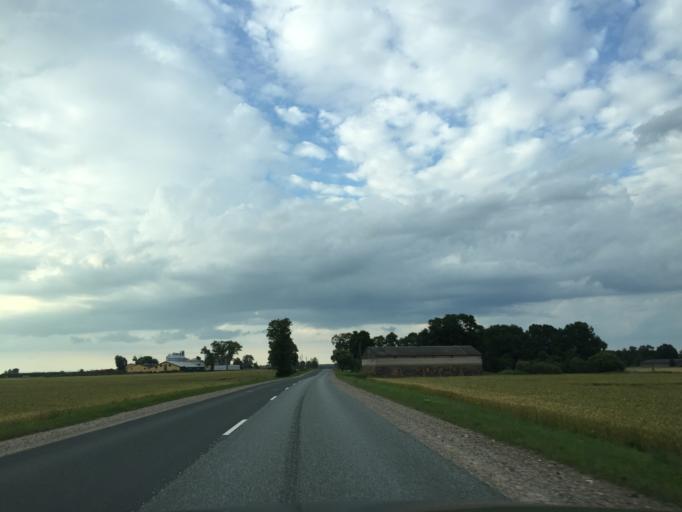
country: LV
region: Dobeles Rajons
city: Dobele
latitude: 56.7173
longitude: 23.3833
